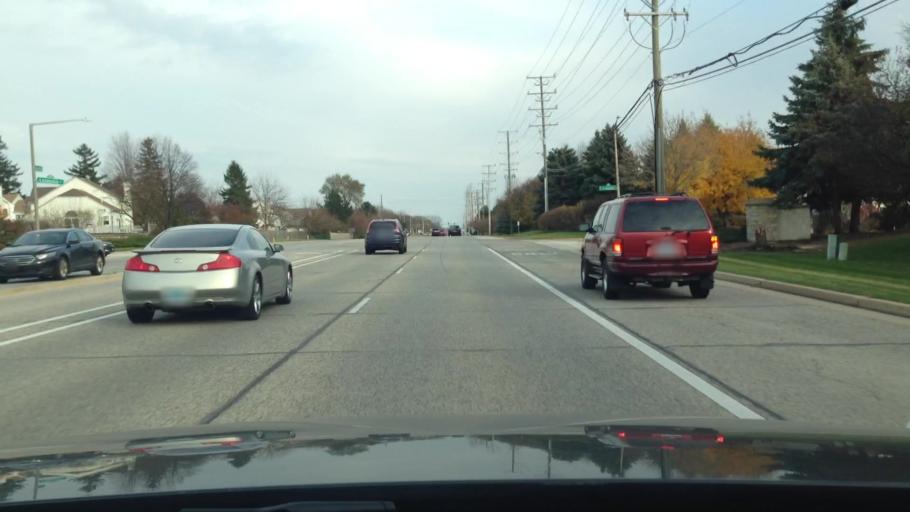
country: US
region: Illinois
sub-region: McHenry County
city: Huntley
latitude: 42.1756
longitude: -88.3907
